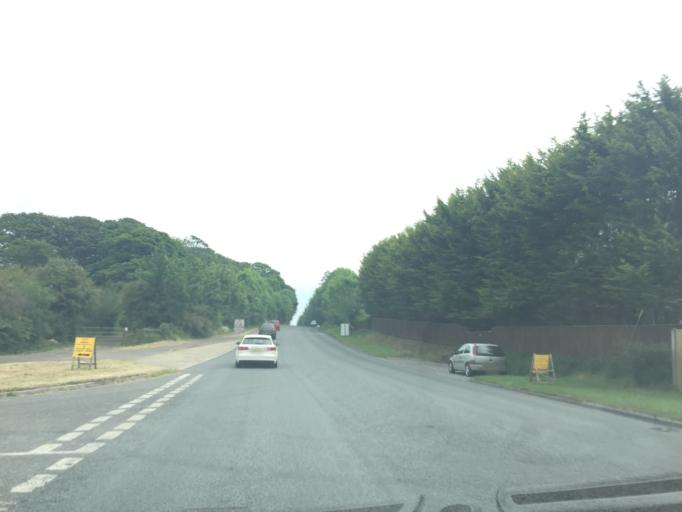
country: GB
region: England
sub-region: Dorset
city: Bovington Camp
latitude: 50.6648
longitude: -2.3298
